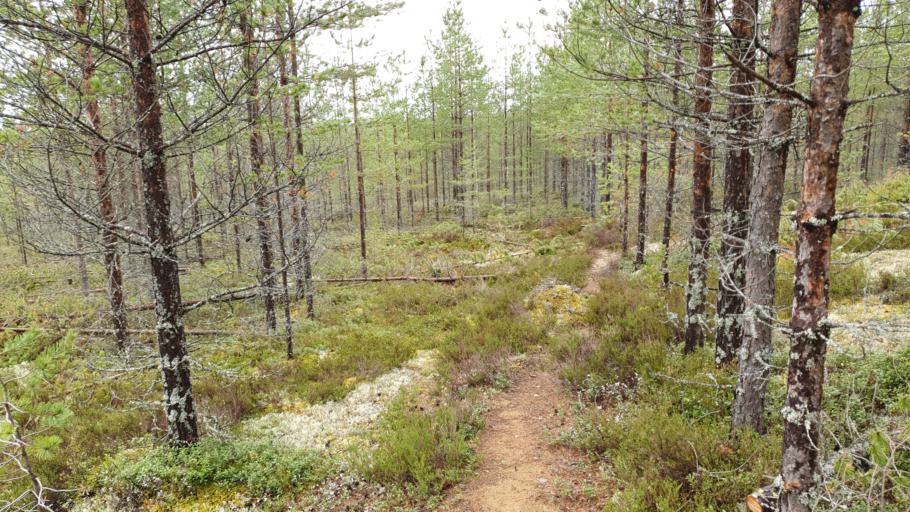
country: FI
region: Kainuu
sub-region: Kehys-Kainuu
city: Kuhmo
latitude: 64.1505
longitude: 29.3989
